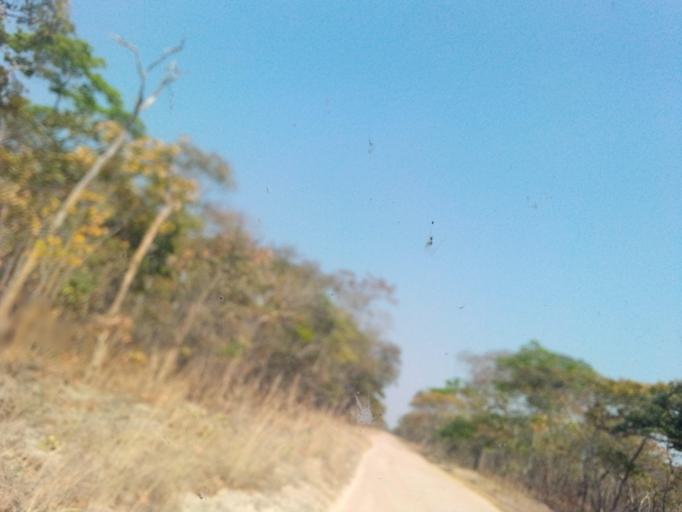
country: ZM
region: Northern
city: Mpika
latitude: -12.2282
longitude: 30.9115
